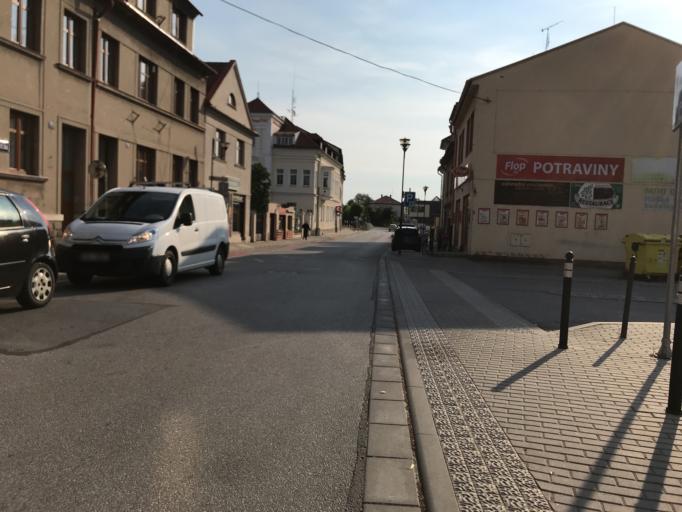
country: CZ
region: Jihocesky
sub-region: Okres Jindrichuv Hradec
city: Trebon
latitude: 49.0043
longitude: 14.7726
